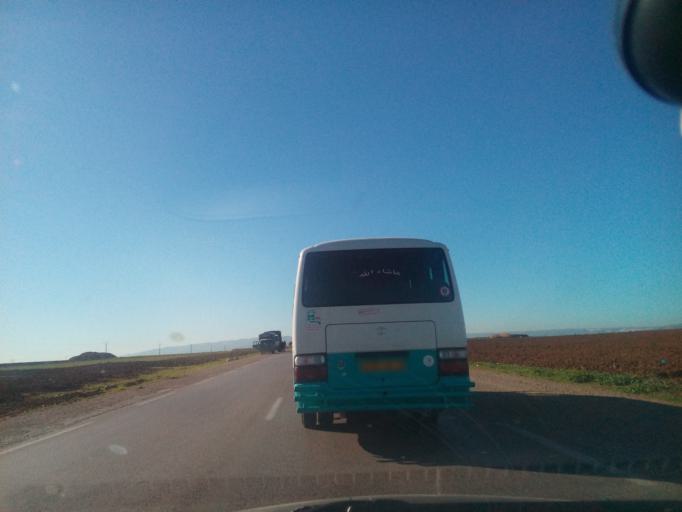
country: DZ
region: Relizane
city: Relizane
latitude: 35.8930
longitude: 0.6372
